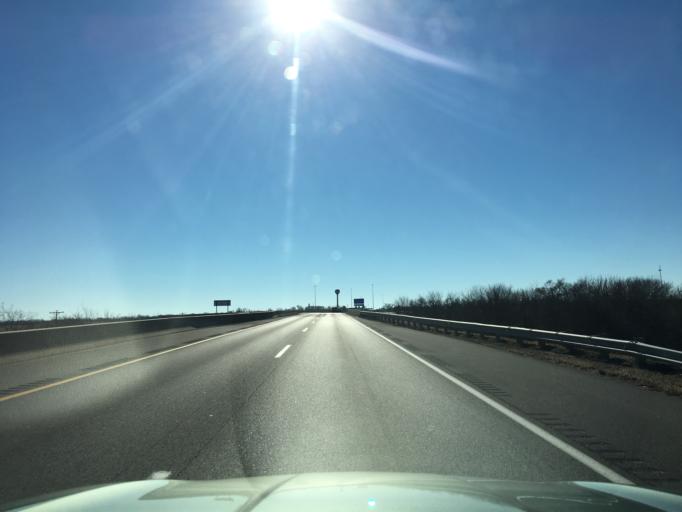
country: US
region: Kansas
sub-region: Sumner County
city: Belle Plaine
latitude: 37.3755
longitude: -97.3233
